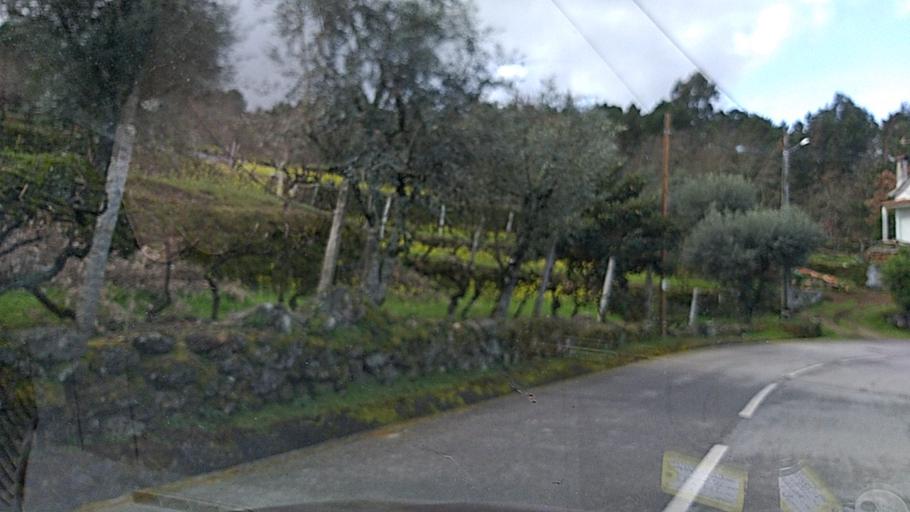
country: PT
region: Guarda
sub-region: Fornos de Algodres
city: Fornos de Algodres
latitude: 40.6630
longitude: -7.6065
